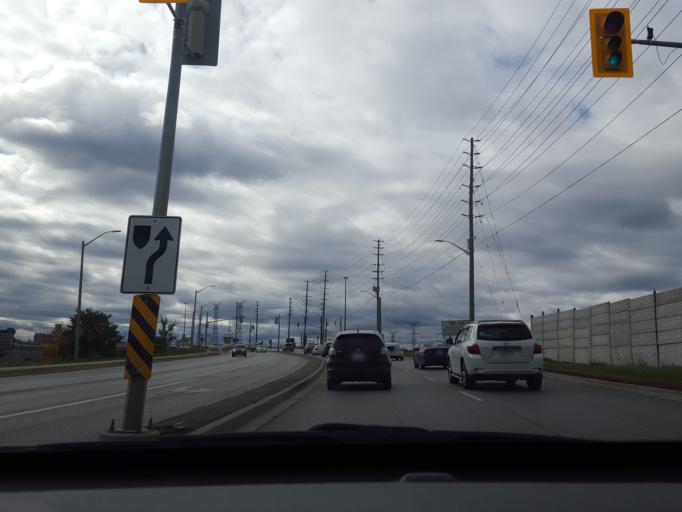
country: CA
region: Ontario
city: Markham
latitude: 43.8533
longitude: -79.3076
